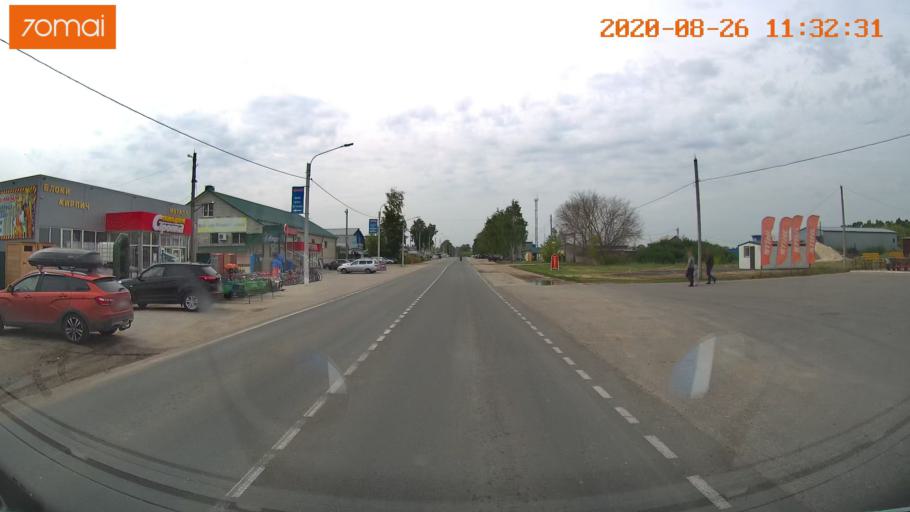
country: RU
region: Rjazan
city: Shilovo
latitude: 54.3016
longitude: 40.8644
